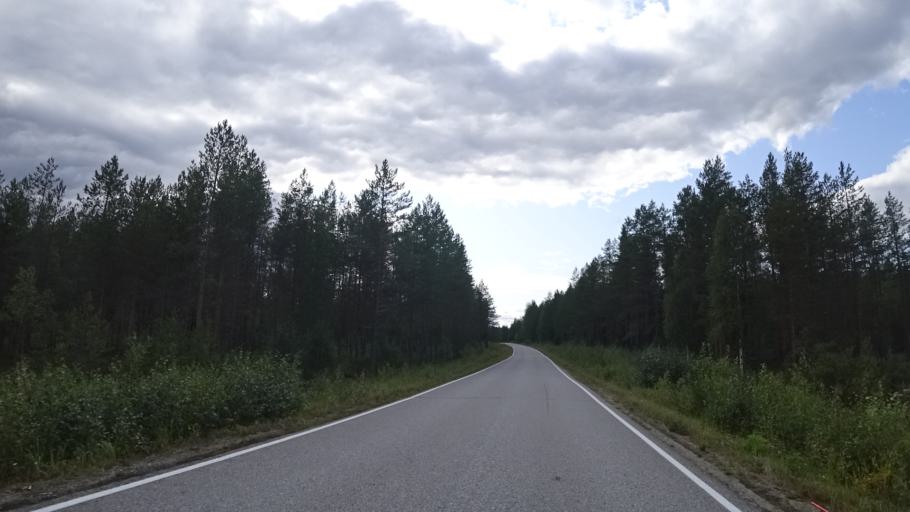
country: FI
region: North Karelia
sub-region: Joensuu
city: Ilomantsi
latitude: 62.4369
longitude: 31.0663
